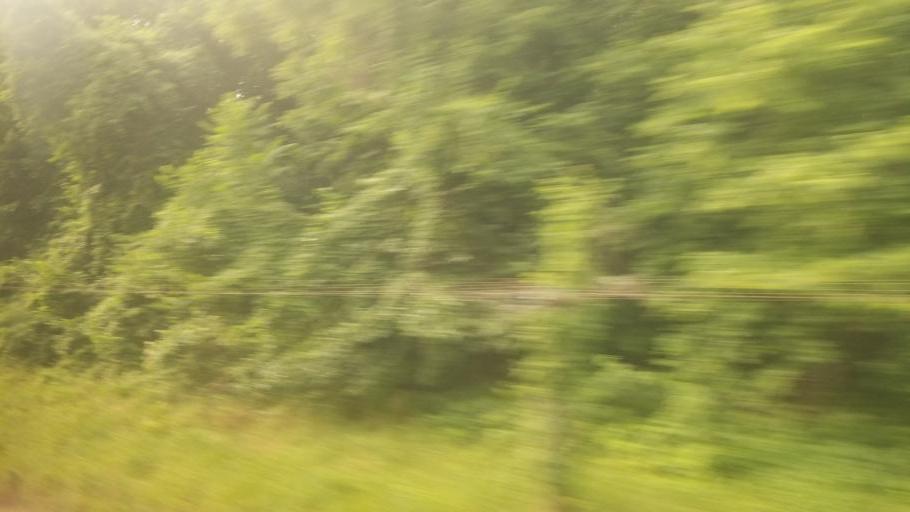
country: US
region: Kansas
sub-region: Jefferson County
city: Oskaloosa
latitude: 39.0588
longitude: -95.4155
